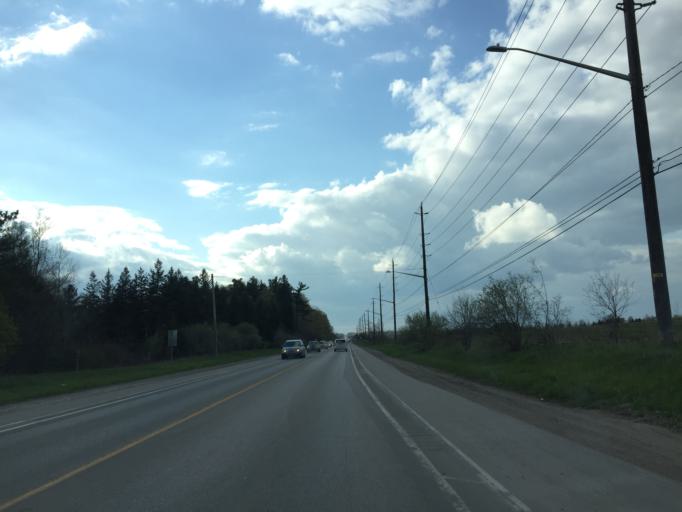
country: CA
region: Ontario
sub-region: Wellington County
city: Guelph
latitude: 43.5413
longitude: -80.2091
